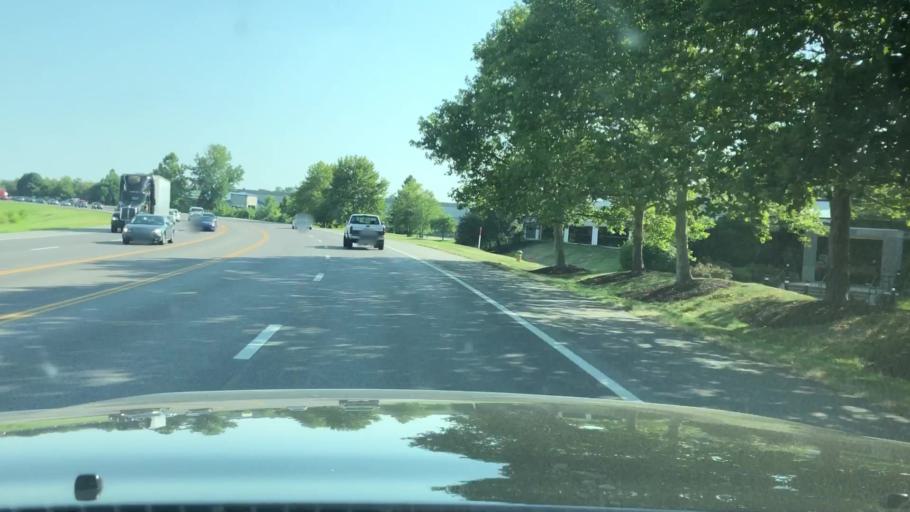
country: US
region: Missouri
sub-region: Saint Charles County
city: Saint Charles
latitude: 38.7871
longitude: -90.4587
